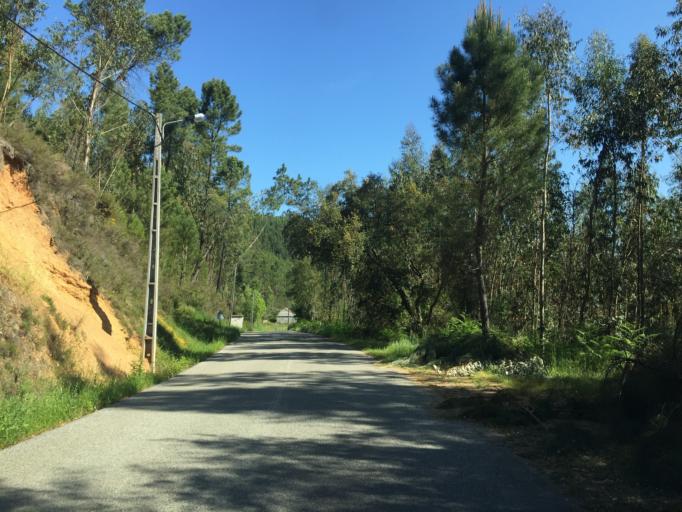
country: PT
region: Coimbra
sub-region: Pampilhosa da Serra
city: Pampilhosa da Serra
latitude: 40.0483
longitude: -7.8112
